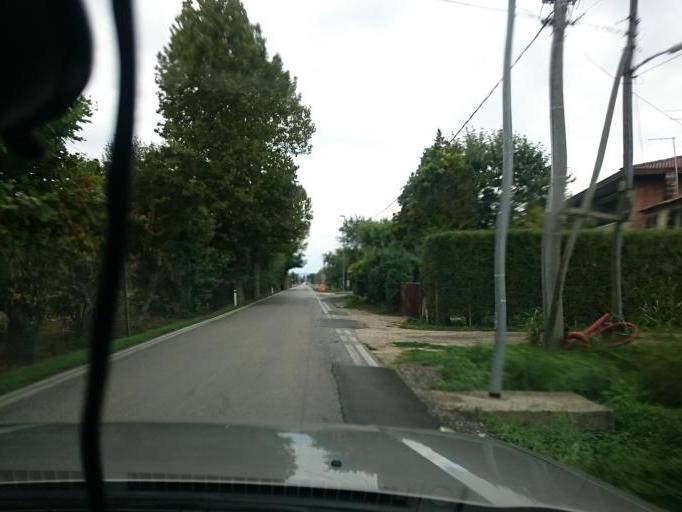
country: IT
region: Veneto
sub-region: Provincia di Padova
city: Mestrino
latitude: 45.4274
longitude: 11.7470
